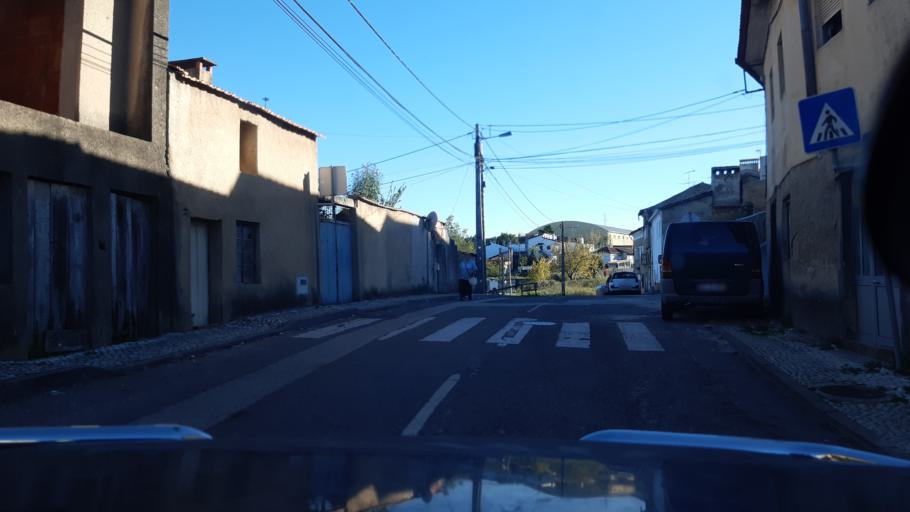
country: PT
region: Aveiro
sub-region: Agueda
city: Agueda
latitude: 40.5605
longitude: -8.4416
